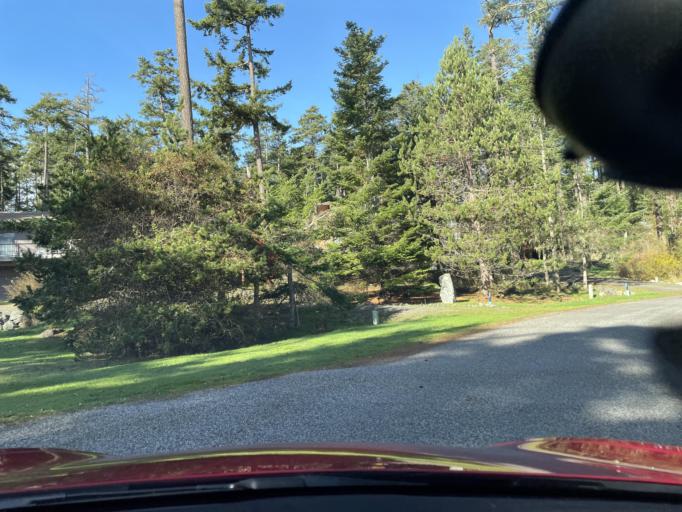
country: US
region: Washington
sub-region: San Juan County
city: Friday Harbor
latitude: 48.4612
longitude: -122.9634
